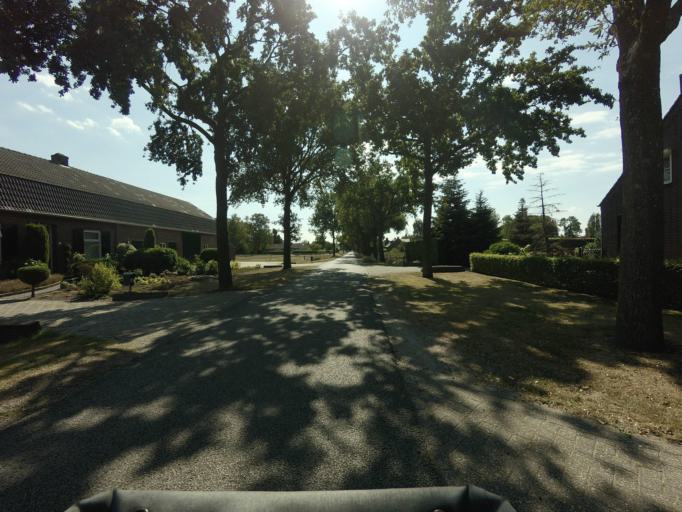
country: NL
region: North Brabant
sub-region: Gemeente Someren
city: Someren
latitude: 51.3485
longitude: 5.6666
